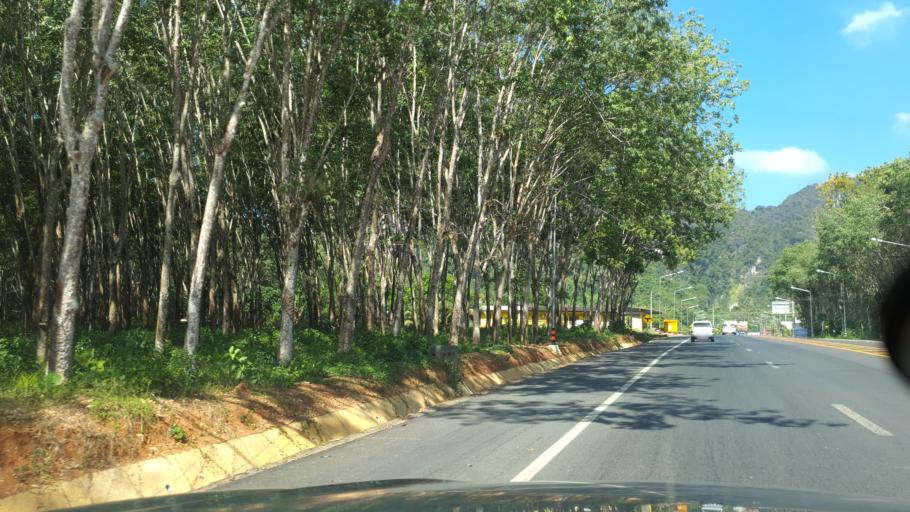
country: TH
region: Krabi
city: Krabi
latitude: 8.0765
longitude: 98.8577
